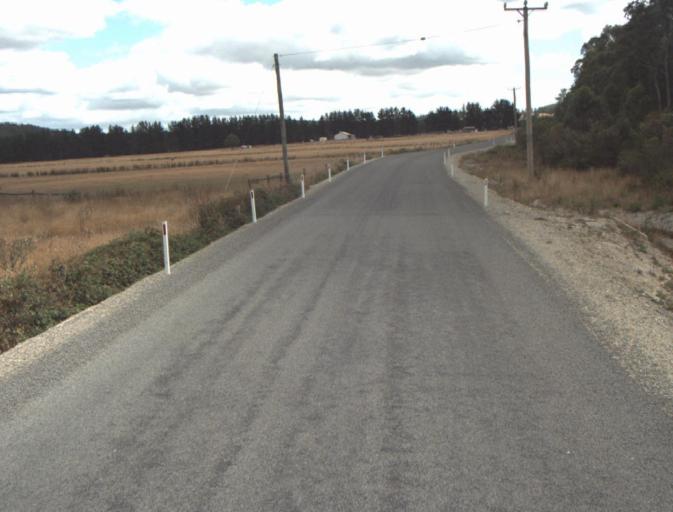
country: AU
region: Tasmania
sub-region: Launceston
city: Mayfield
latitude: -41.2137
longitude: 147.1903
